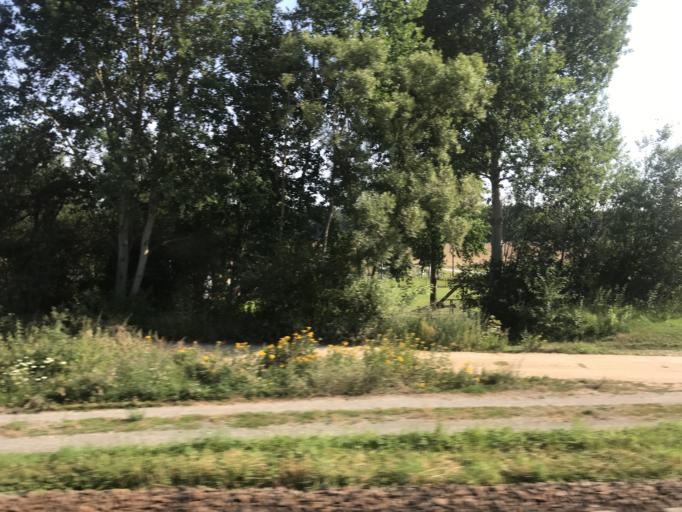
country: CZ
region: Jihocesky
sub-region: Okres Tabor
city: Tabor
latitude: 49.4327
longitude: 14.6729
